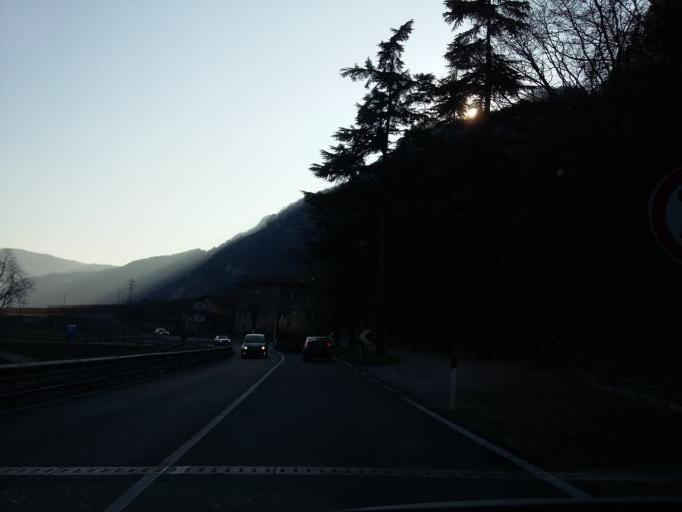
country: IT
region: Trentino-Alto Adige
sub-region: Provincia di Trento
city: Nago-Torbole
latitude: 45.8585
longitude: 10.9200
